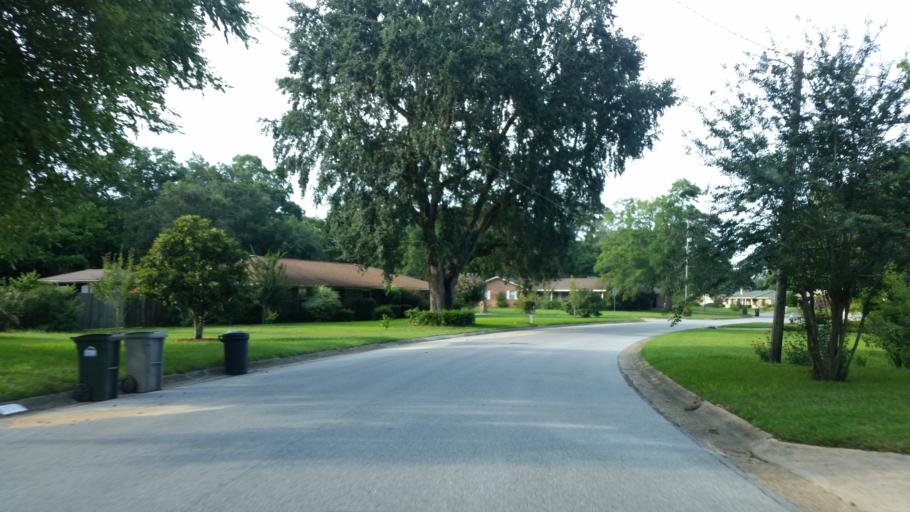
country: US
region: Florida
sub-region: Escambia County
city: Ferry Pass
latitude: 30.5135
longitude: -87.1896
